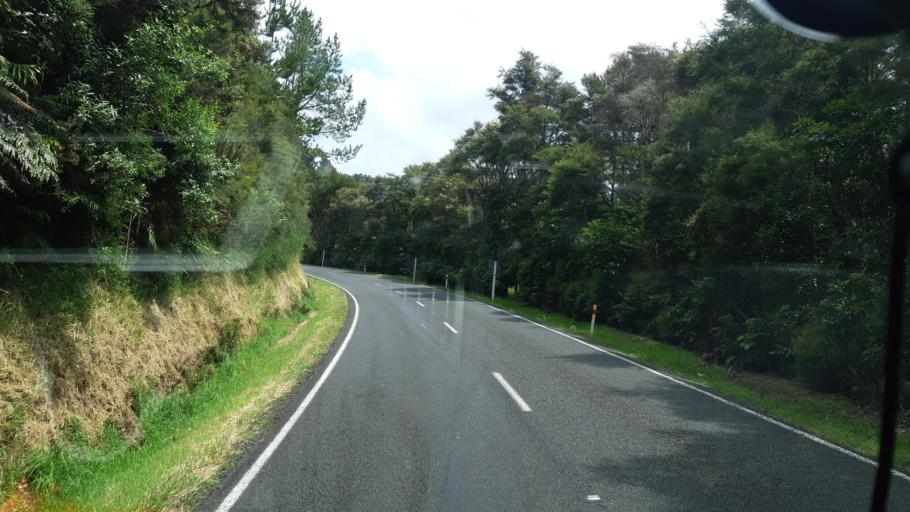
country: NZ
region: Waikato
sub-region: South Waikato District
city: Tokoroa
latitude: -38.2730
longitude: 175.6744
